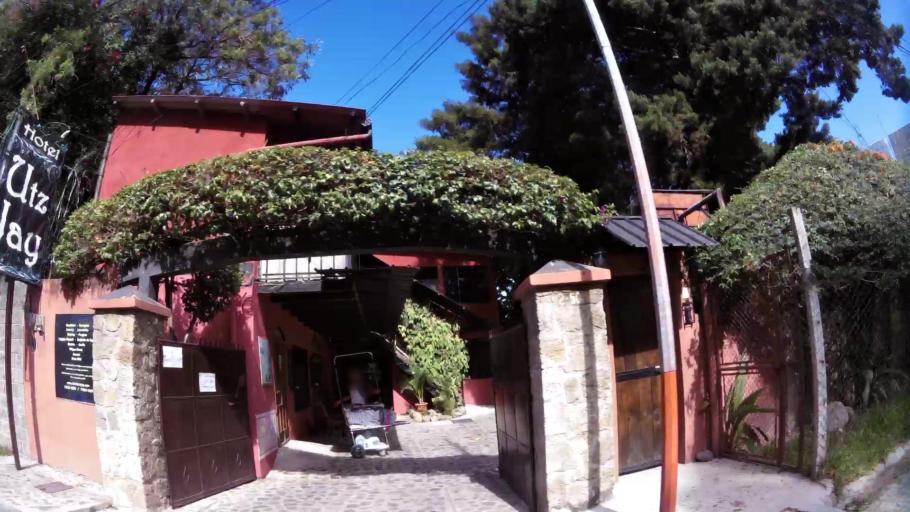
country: GT
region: Solola
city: Panajachel
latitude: 14.7393
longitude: -91.1589
